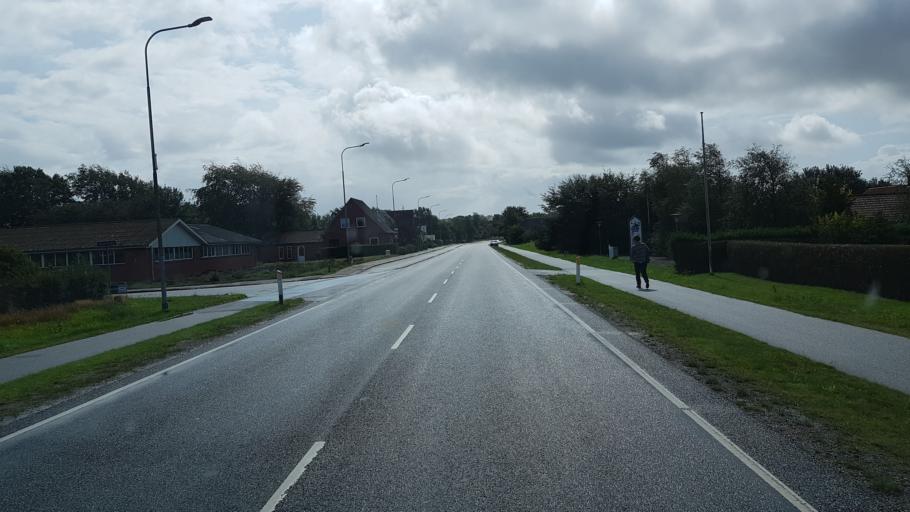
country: DK
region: South Denmark
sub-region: Vejen Kommune
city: Holsted
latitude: 55.4912
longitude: 8.9147
